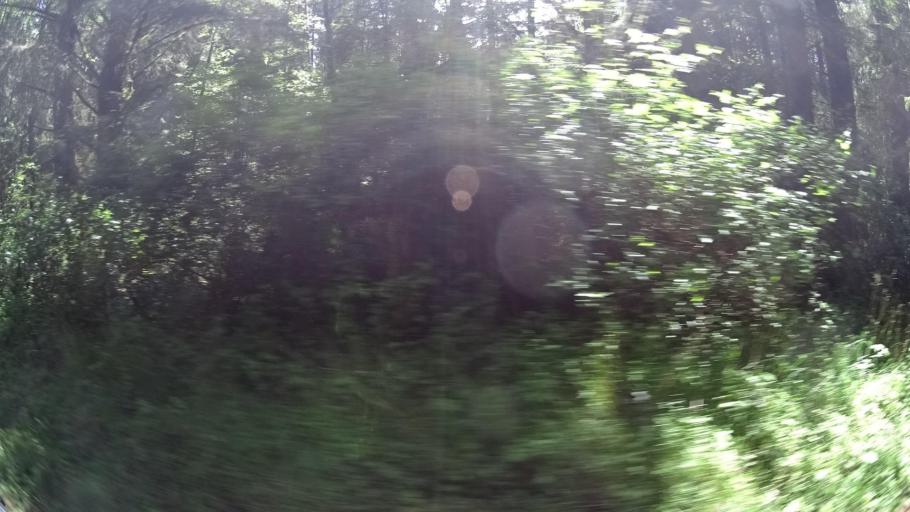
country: US
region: California
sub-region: Humboldt County
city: McKinleyville
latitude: 40.9632
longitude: -124.0706
